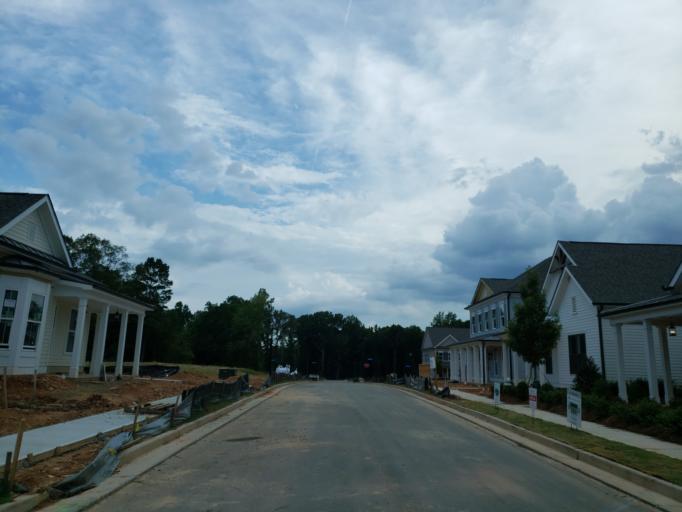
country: US
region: Georgia
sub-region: Cherokee County
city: Holly Springs
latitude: 34.1796
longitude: -84.4346
